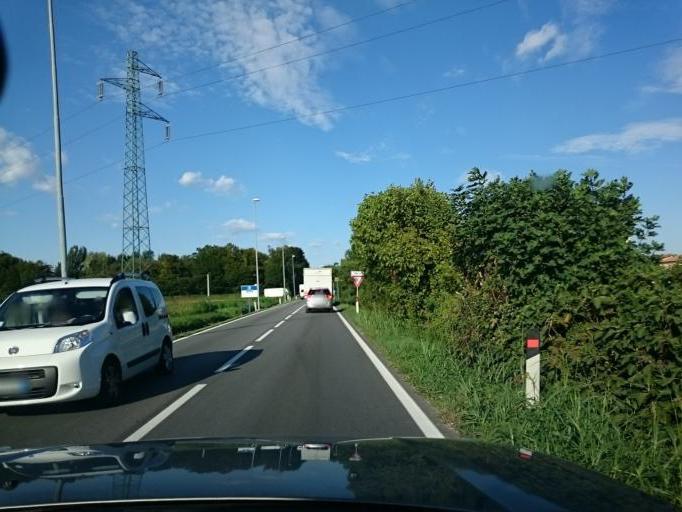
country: IT
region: Veneto
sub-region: Provincia di Padova
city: Abano Terme
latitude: 45.3537
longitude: 11.8073
